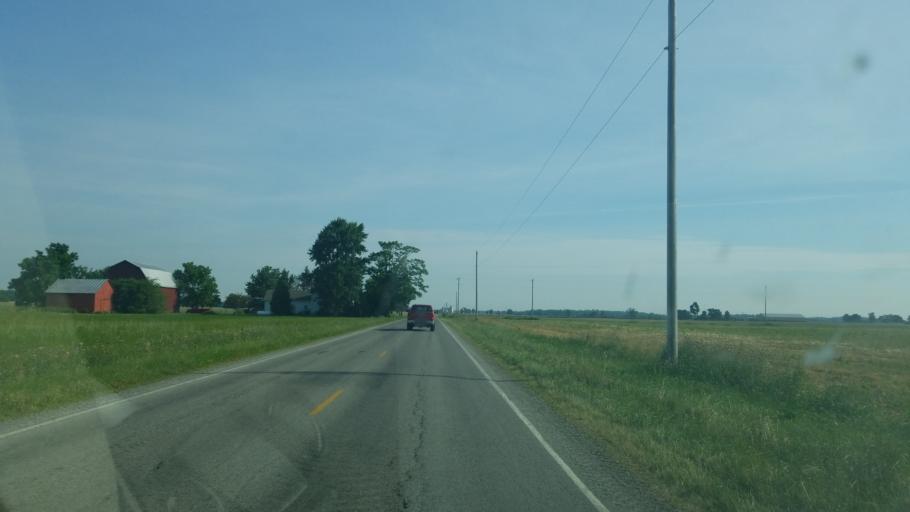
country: US
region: Ohio
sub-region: Hancock County
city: Arlington
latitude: 40.9563
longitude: -83.6986
